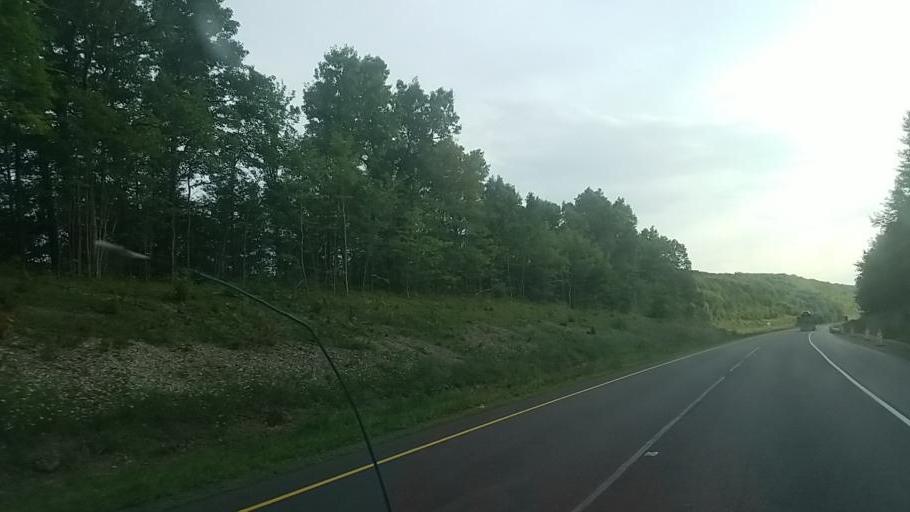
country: US
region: Pennsylvania
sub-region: Centre County
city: Milesburg
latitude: 41.0097
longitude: -77.9645
